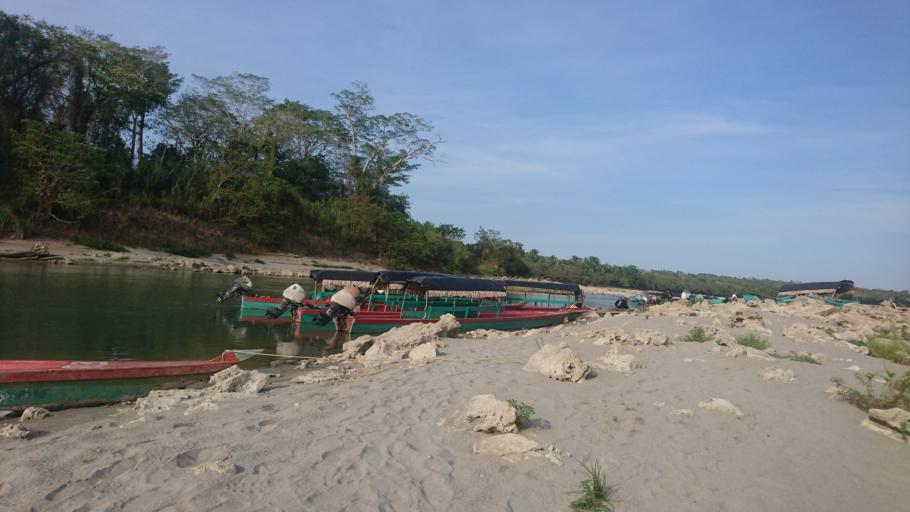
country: MX
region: Chiapas
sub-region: Ocosingo
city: Frontera Corozal
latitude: 16.8245
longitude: -90.8862
